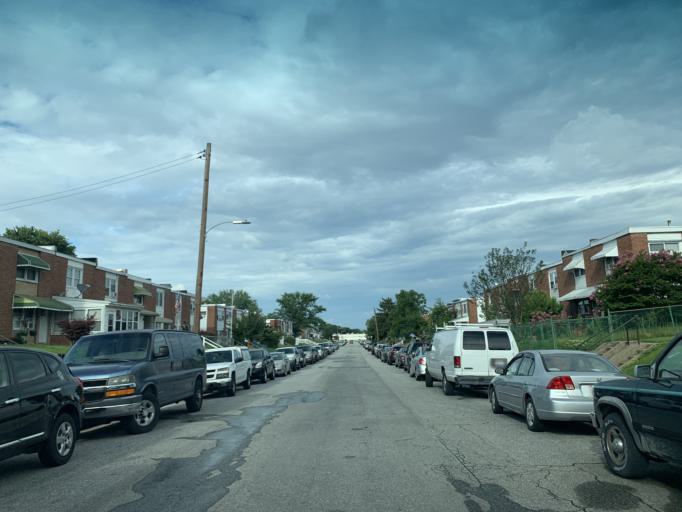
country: US
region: Maryland
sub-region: Baltimore County
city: Rosedale
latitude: 39.2966
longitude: -76.5148
